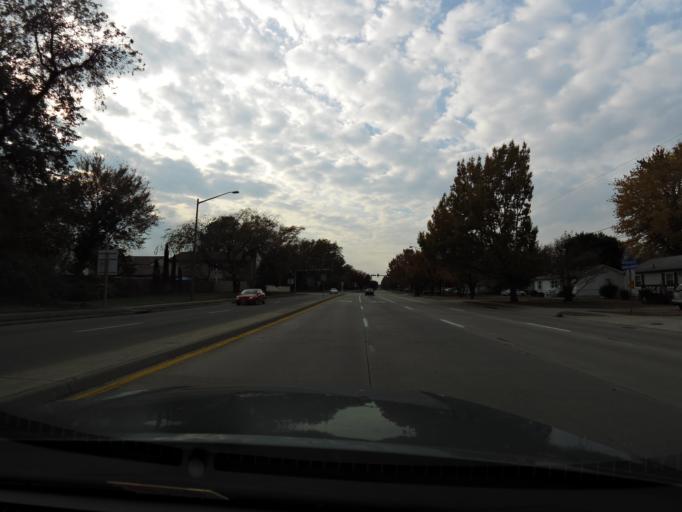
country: US
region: Virginia
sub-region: City of Hampton
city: Hampton
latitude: 37.0244
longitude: -76.3510
